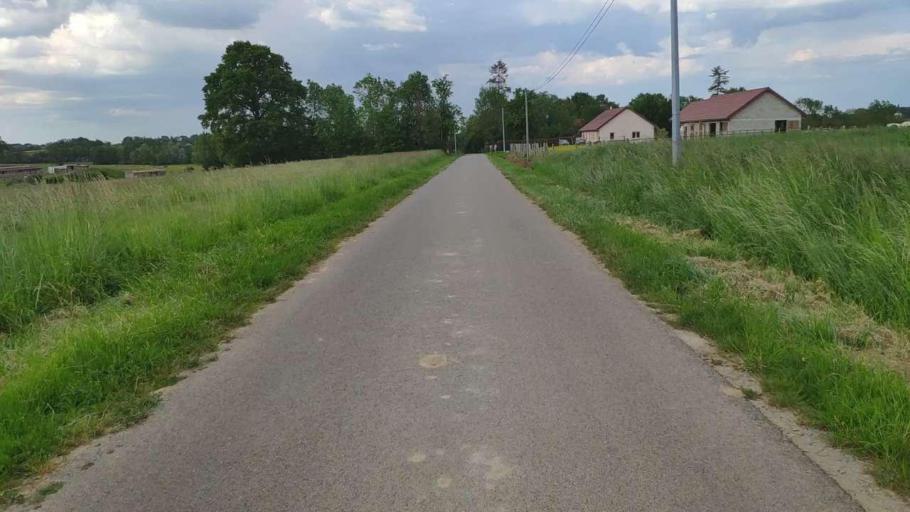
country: FR
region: Franche-Comte
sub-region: Departement du Jura
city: Bletterans
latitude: 46.7991
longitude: 5.3676
